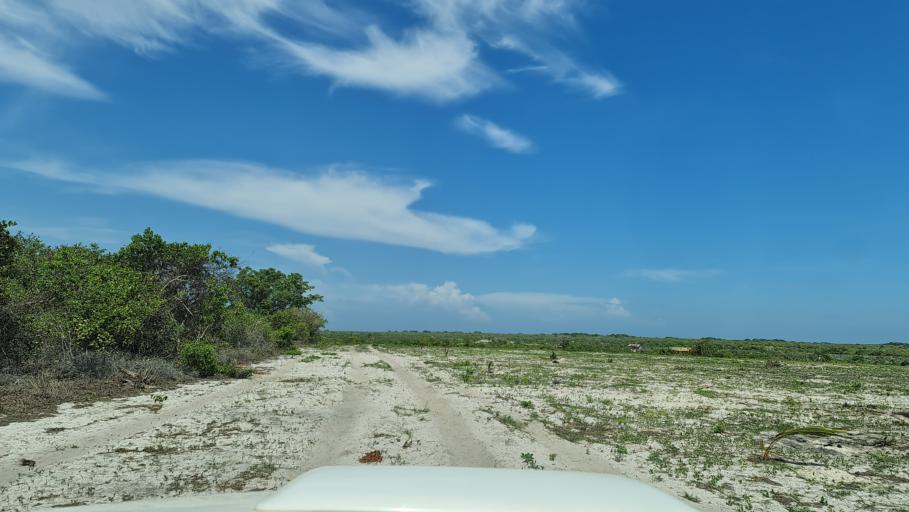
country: MZ
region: Nampula
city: Ilha de Mocambique
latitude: -15.1957
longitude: 40.6177
